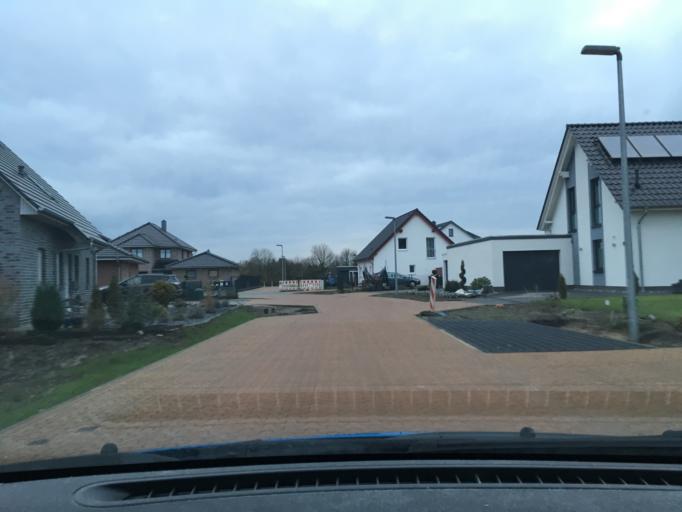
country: DE
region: Lower Saxony
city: Celle
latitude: 52.6421
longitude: 10.0416
